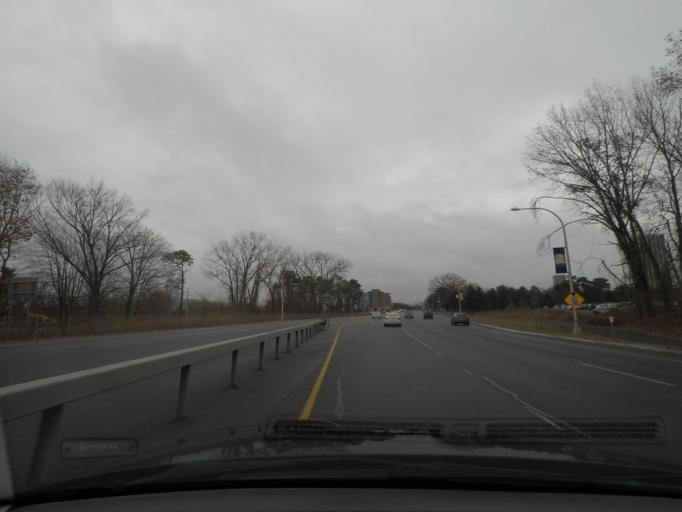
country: US
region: New York
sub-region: Albany County
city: Roessleville
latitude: 42.6923
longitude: -73.8266
